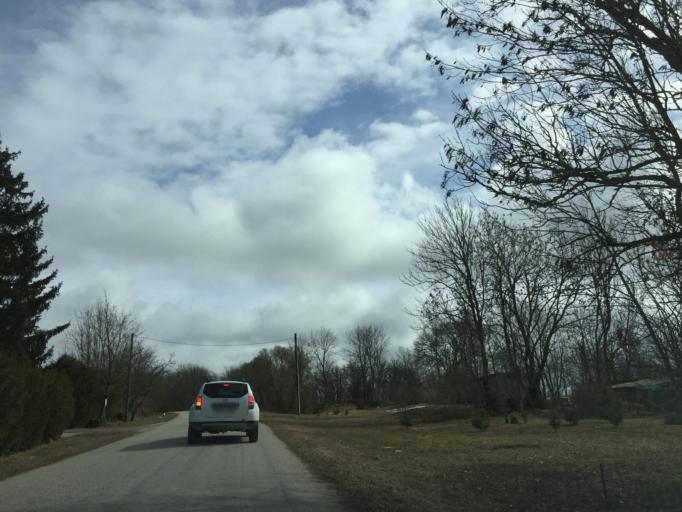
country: EE
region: Laeaene
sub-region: Lihula vald
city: Lihula
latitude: 58.7364
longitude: 23.8365
